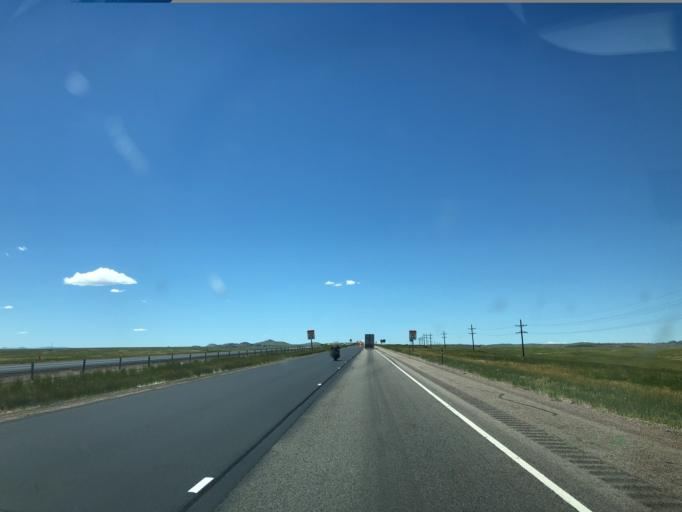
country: US
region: Wyoming
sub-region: Laramie County
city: Cheyenne
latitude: 41.1000
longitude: -105.0843
